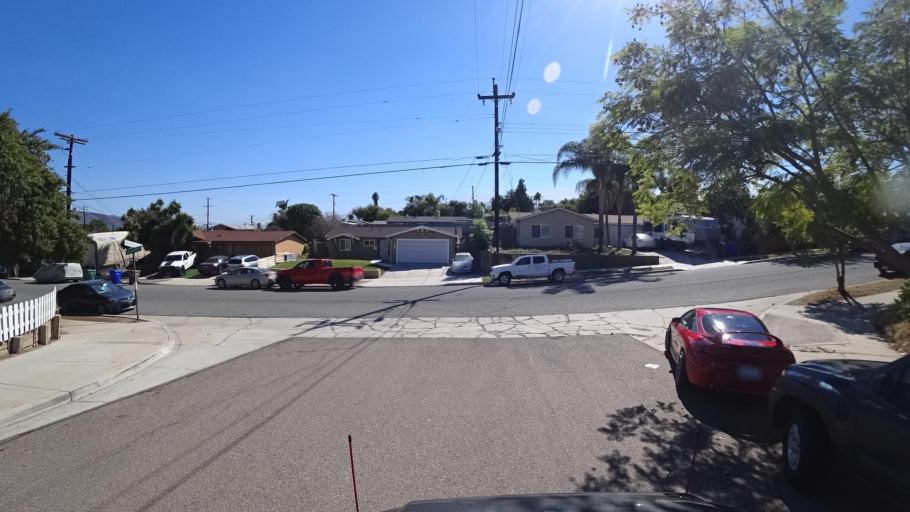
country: US
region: California
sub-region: San Diego County
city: La Presa
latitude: 32.7130
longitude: -117.0180
